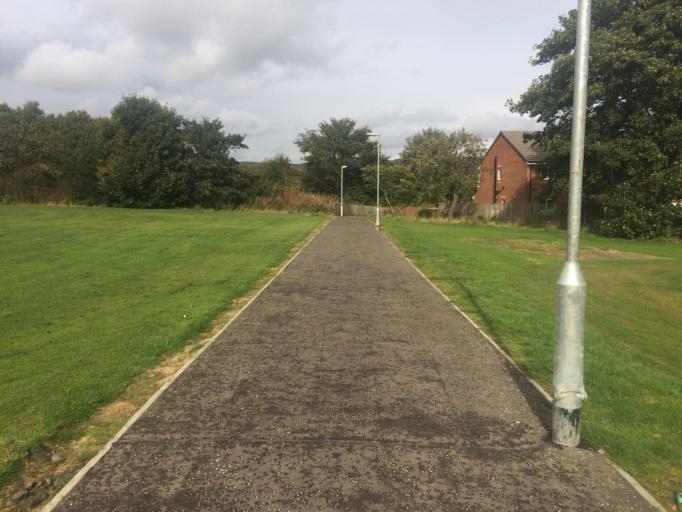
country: GB
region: Scotland
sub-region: Fife
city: Kelty
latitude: 56.1365
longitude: -3.3779
